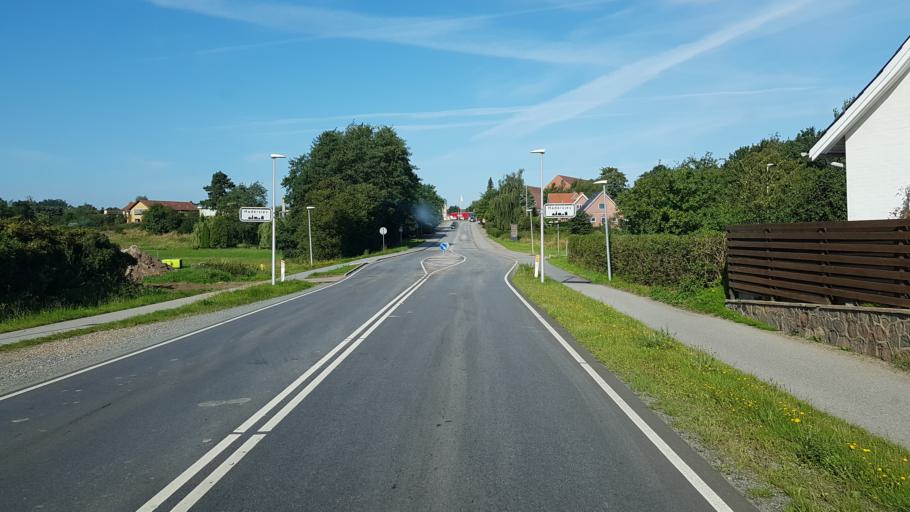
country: DK
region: South Denmark
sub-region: Haderslev Kommune
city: Haderslev
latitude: 55.2435
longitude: 9.5085
